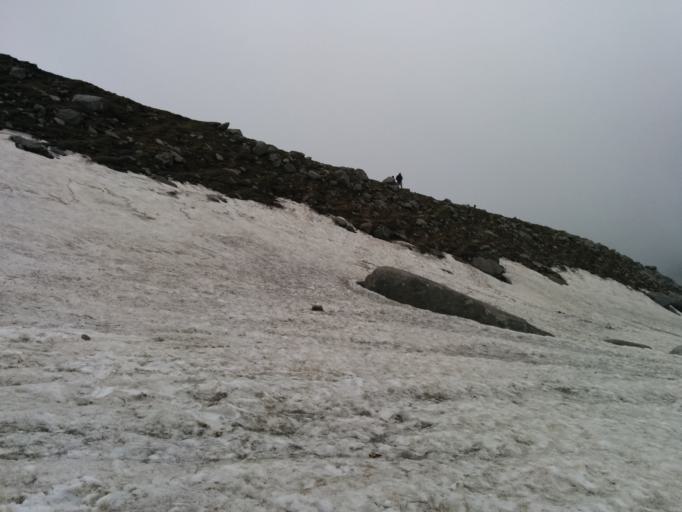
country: IN
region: Himachal Pradesh
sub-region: Kangra
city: Dharmsala
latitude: 32.2842
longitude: 76.3676
